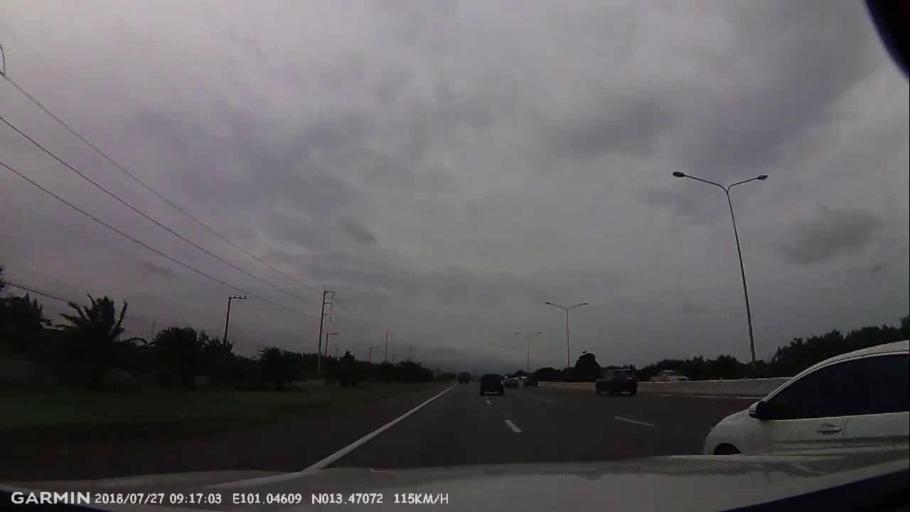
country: TH
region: Chon Buri
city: Phan Thong
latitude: 13.4703
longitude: 101.0461
